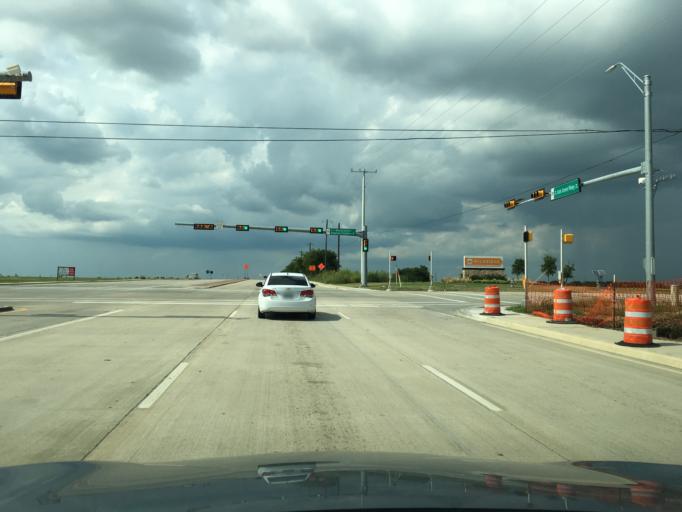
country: US
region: Texas
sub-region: Denton County
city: Oak Point
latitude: 33.1863
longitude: -96.9769
